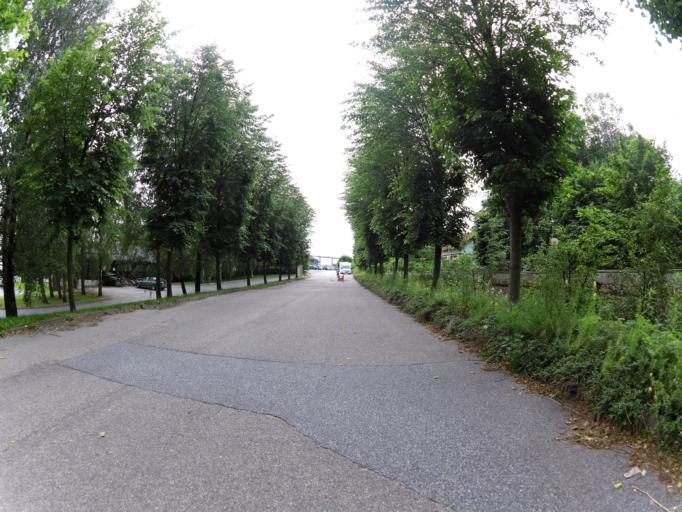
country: NO
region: Ostfold
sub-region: Fredrikstad
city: Fredrikstad
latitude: 59.2166
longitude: 10.9619
